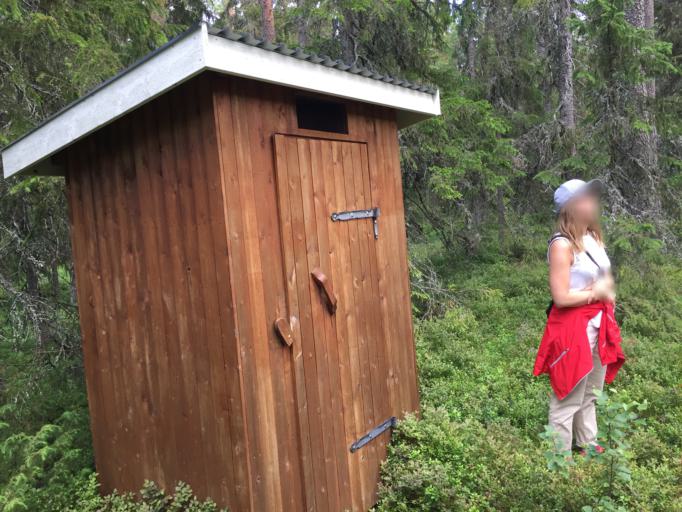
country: SE
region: Dalarna
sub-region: Malung-Saelens kommun
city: Malung
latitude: 60.6405
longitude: 13.7743
